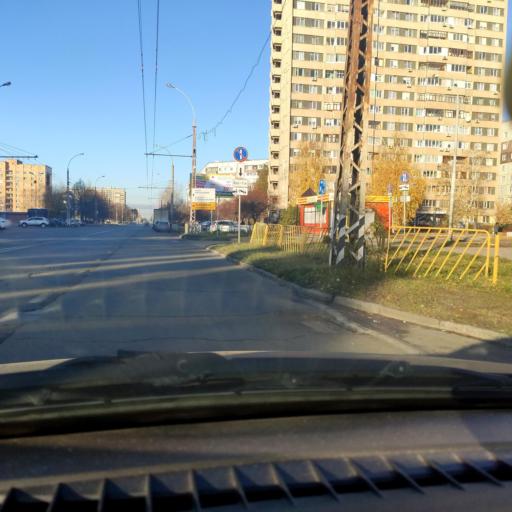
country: RU
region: Samara
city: Tol'yatti
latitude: 53.5343
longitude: 49.3212
